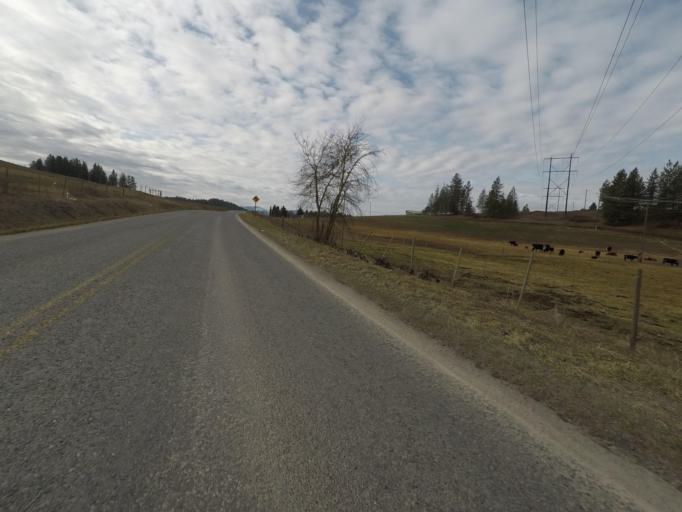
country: US
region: Washington
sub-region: Stevens County
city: Colville
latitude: 48.5257
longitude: -117.8808
